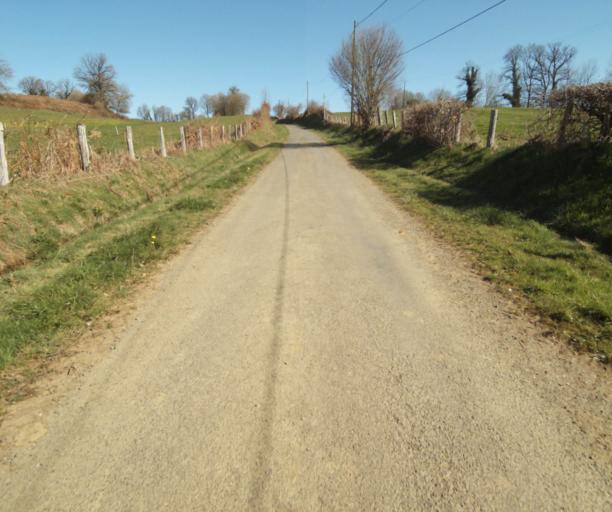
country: FR
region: Limousin
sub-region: Departement de la Correze
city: Seilhac
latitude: 45.3786
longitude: 1.7379
